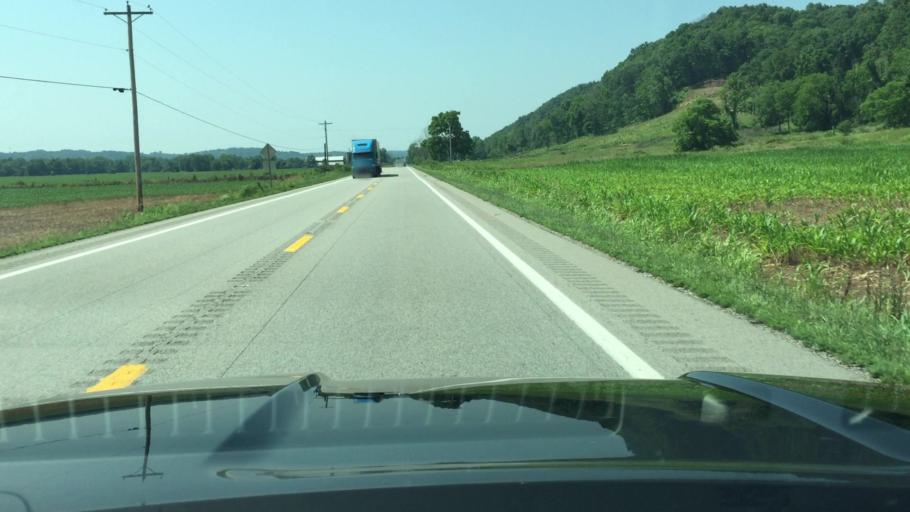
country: US
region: West Virginia
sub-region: Putnam County
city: Buffalo
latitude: 38.6649
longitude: -81.9678
